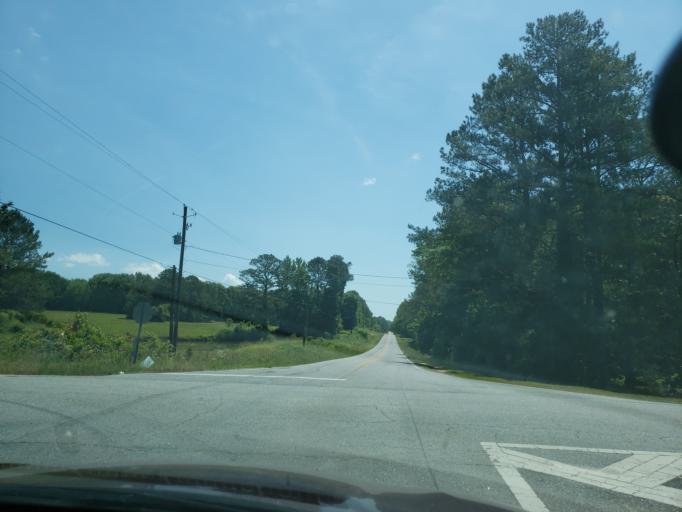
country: US
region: Alabama
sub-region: Elmore County
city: Tallassee
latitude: 32.5807
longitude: -85.8356
